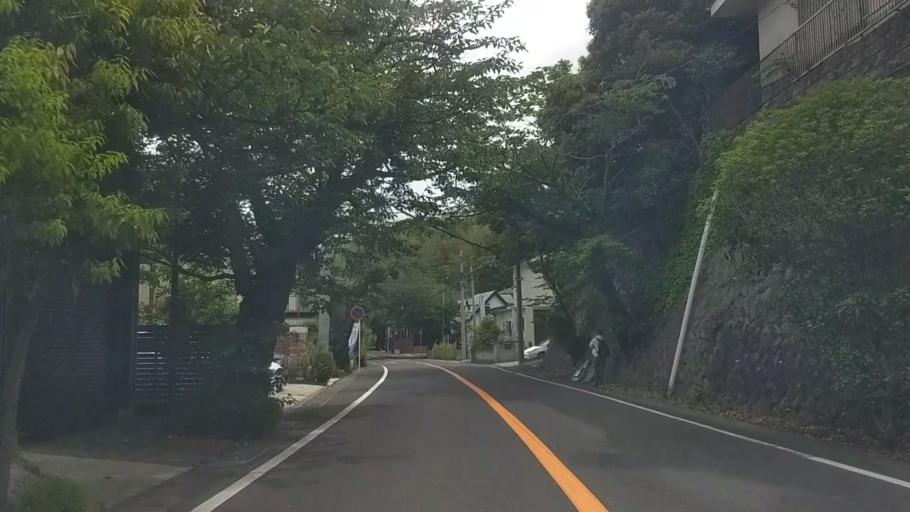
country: JP
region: Kanagawa
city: Kamakura
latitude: 35.3173
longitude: 139.5189
